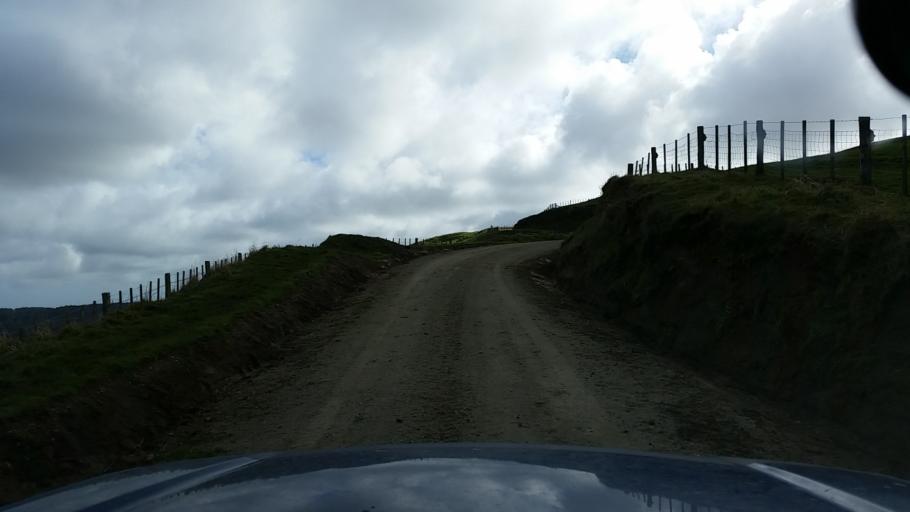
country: NZ
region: Taranaki
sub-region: South Taranaki District
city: Patea
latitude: -39.6691
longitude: 174.5651
